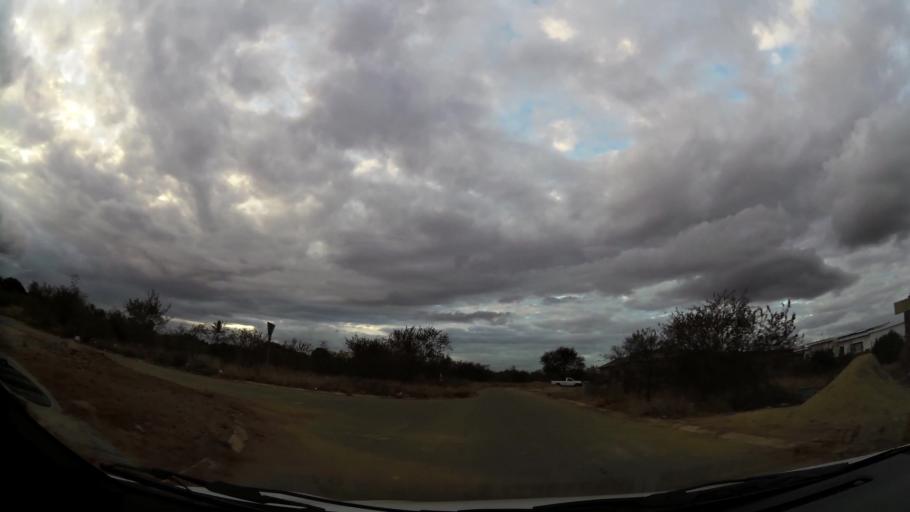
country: ZA
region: Limpopo
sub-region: Waterberg District Municipality
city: Mokopane
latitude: -24.1943
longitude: 28.9981
